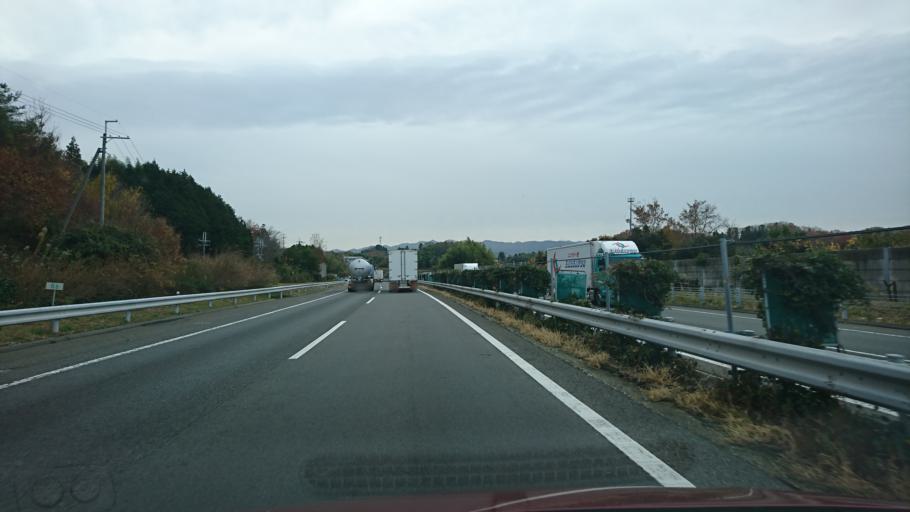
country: JP
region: Hyogo
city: Sandacho
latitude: 34.8279
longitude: 135.1722
